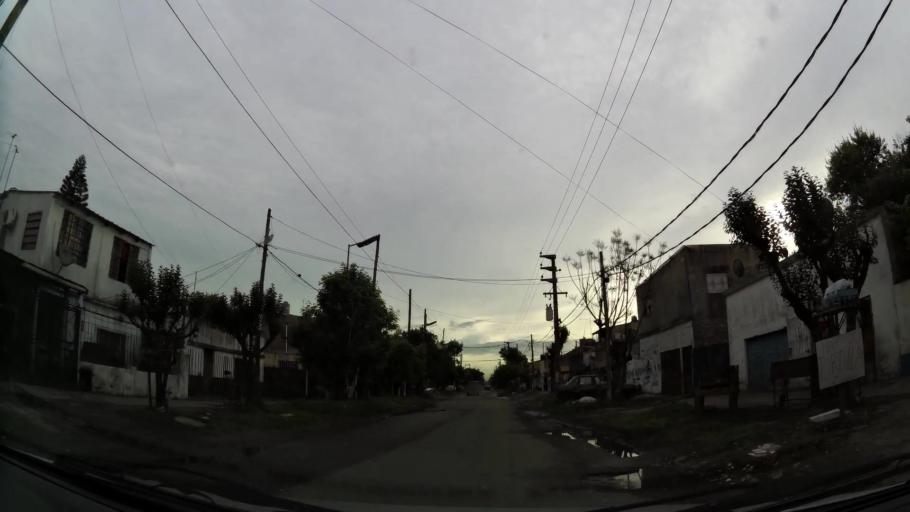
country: AR
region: Buenos Aires
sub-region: Partido de Lanus
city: Lanus
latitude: -34.7273
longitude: -58.3378
